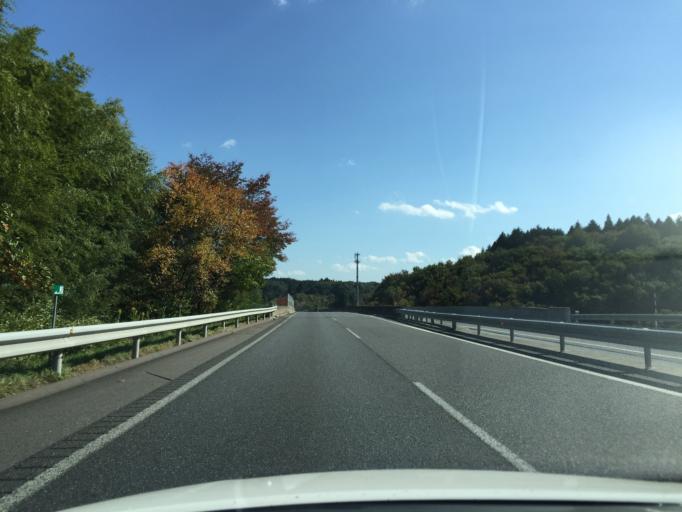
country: JP
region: Fukushima
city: Funehikimachi-funehiki
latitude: 37.2741
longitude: 140.6261
